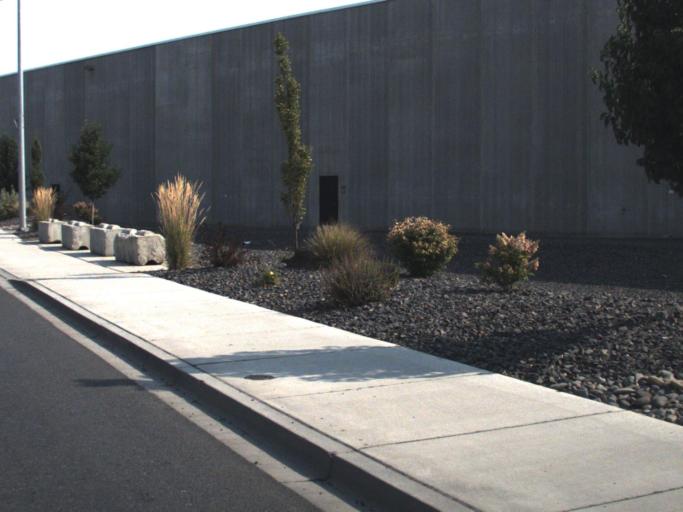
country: US
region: Washington
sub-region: Yakima County
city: Selah
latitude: 46.6499
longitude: -120.5285
